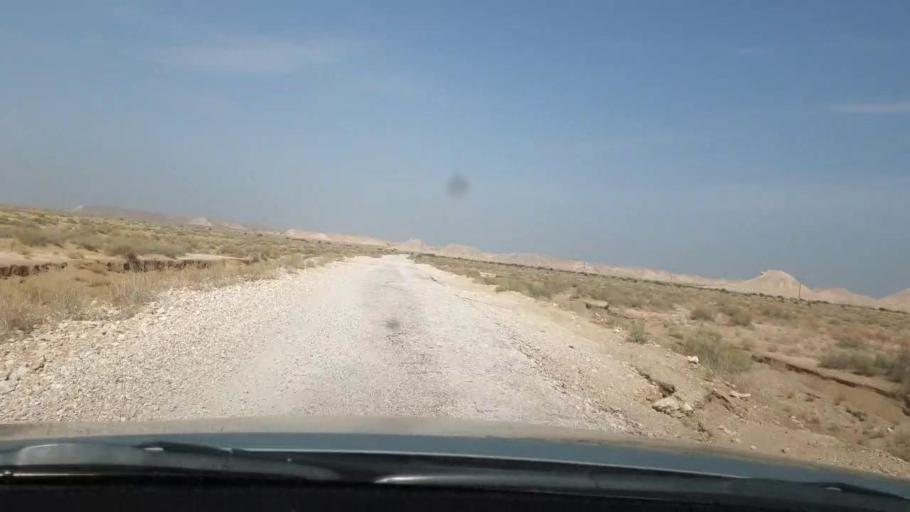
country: PK
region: Sindh
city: Kot Diji
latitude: 27.3273
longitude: 68.8033
